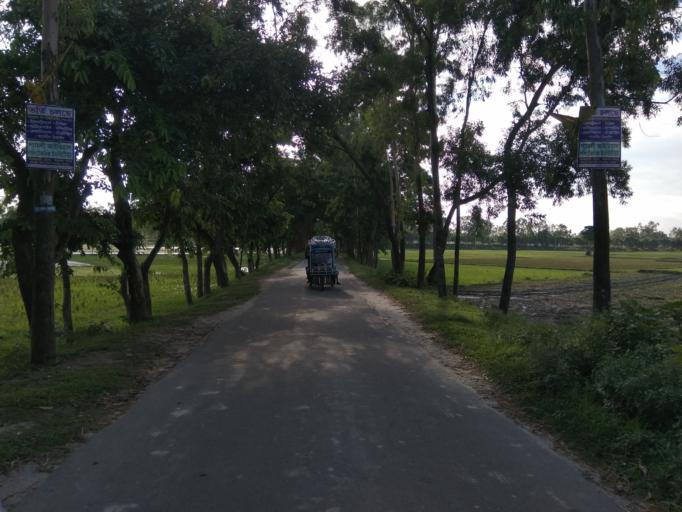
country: BD
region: Rangpur Division
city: Rangpur
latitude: 25.8314
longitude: 89.1159
